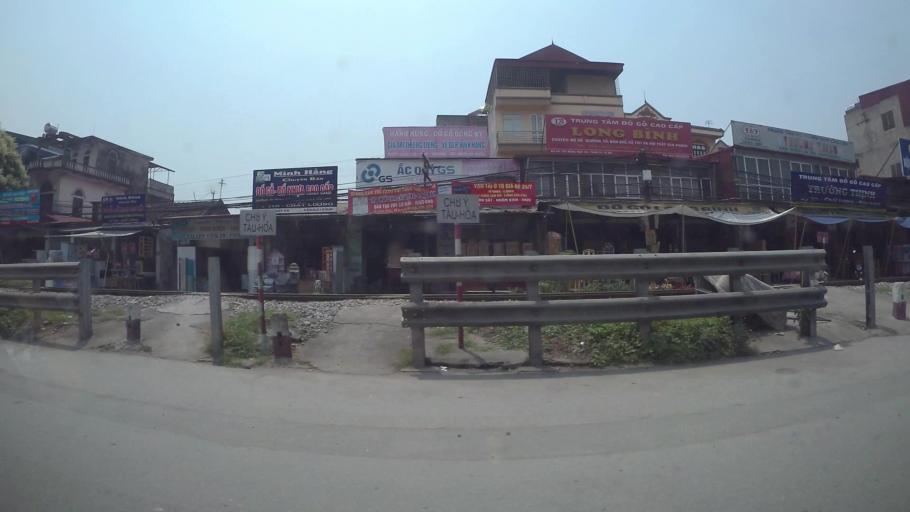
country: VN
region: Ha Noi
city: Van Dien
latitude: 20.9487
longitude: 105.8443
